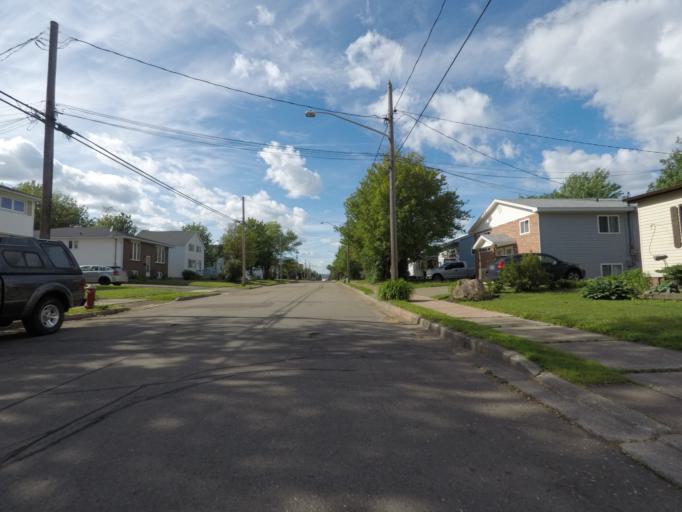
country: CA
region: New Brunswick
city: Moncton
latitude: 46.1005
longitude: -64.8210
